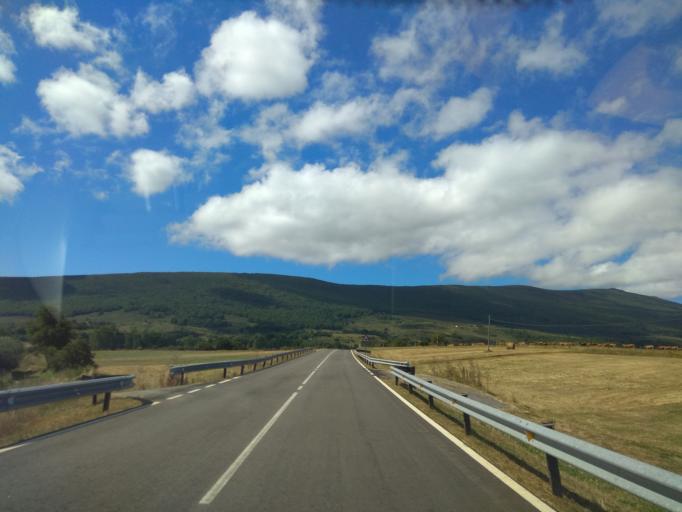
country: ES
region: Cantabria
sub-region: Provincia de Cantabria
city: Villaescusa
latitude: 42.9721
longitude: -4.1590
